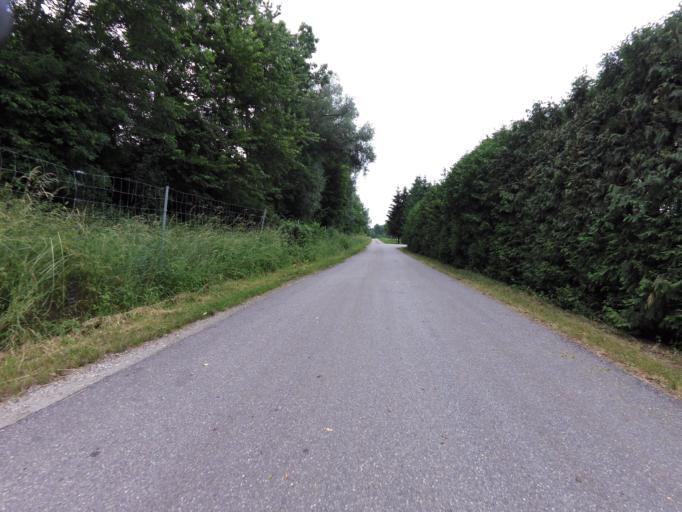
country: DE
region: Bavaria
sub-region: Lower Bavaria
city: Bruckberg
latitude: 48.4902
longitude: 12.0003
